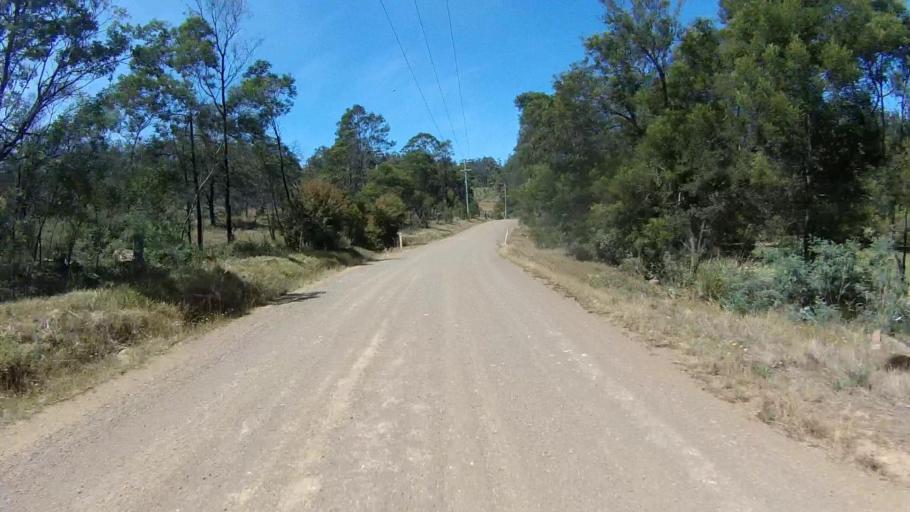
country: AU
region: Tasmania
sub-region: Sorell
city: Sorell
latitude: -42.7673
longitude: 147.6521
